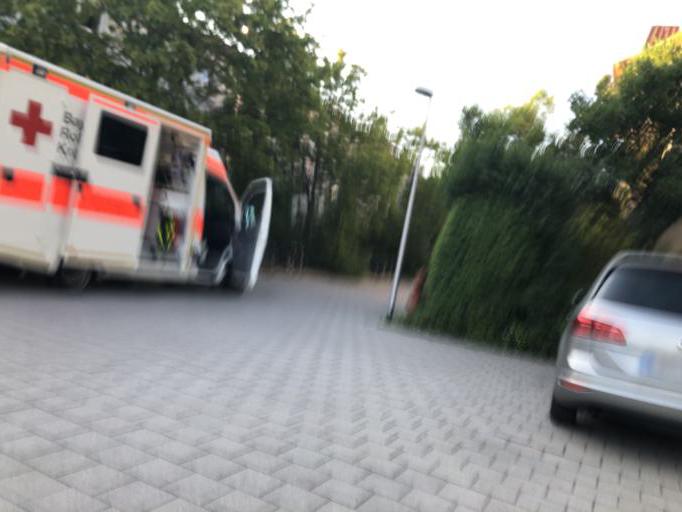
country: DE
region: Bavaria
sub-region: Regierungsbezirk Mittelfranken
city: Erlangen
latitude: 49.5946
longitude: 10.9613
